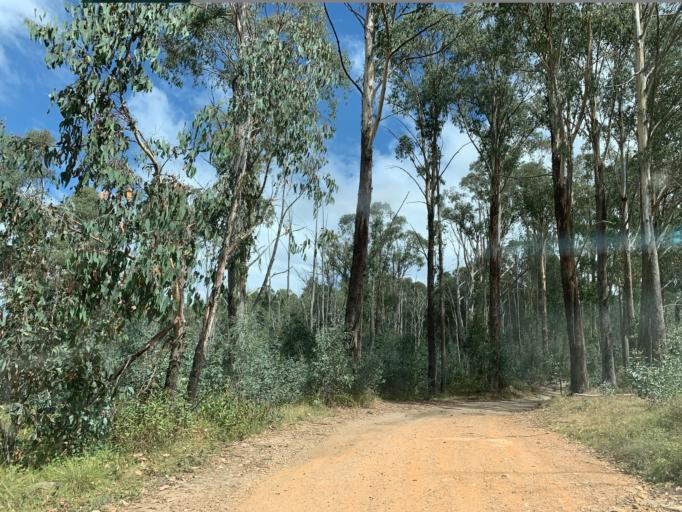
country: AU
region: Victoria
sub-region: Mansfield
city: Mansfield
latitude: -37.1023
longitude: 146.5419
